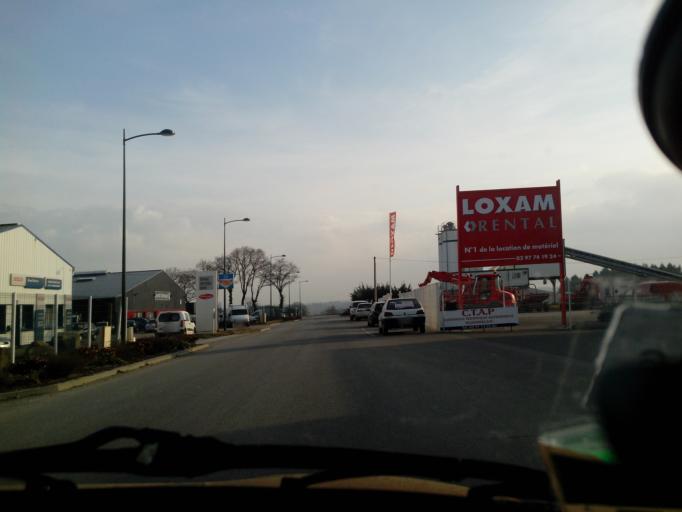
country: FR
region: Brittany
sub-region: Departement du Morbihan
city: Ploermel
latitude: 47.9324
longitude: -2.3758
